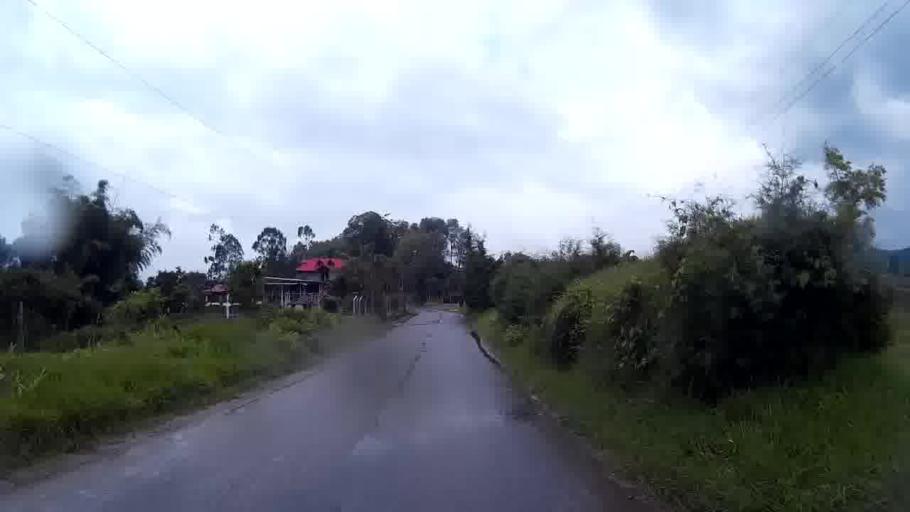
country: CO
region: Quindio
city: Filandia
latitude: 4.6765
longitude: -75.6523
